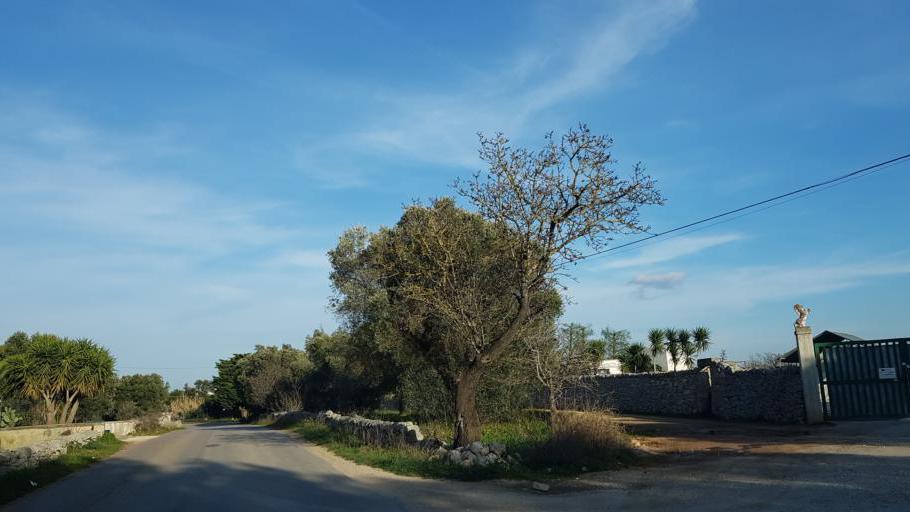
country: IT
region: Apulia
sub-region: Provincia di Brindisi
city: Carovigno
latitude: 40.7033
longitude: 17.6815
